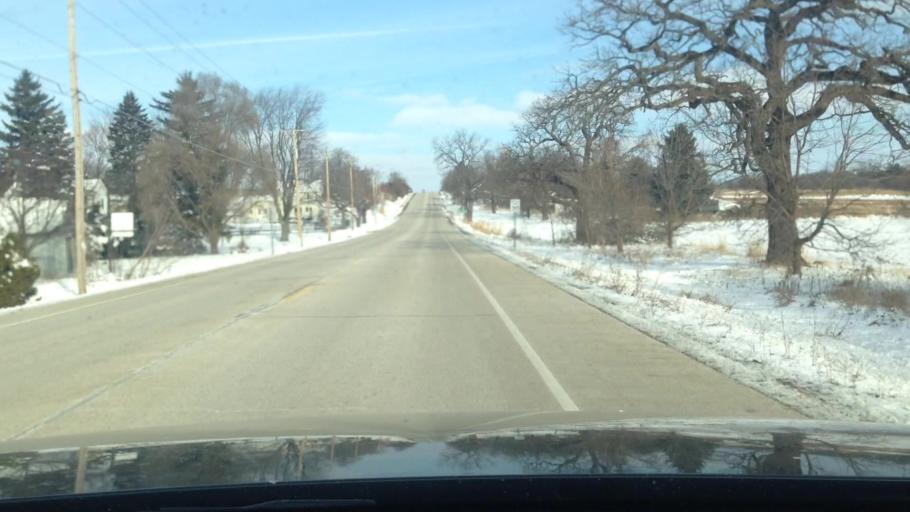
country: US
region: Wisconsin
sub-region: Walworth County
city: Lake Geneva
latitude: 42.6448
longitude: -88.4136
